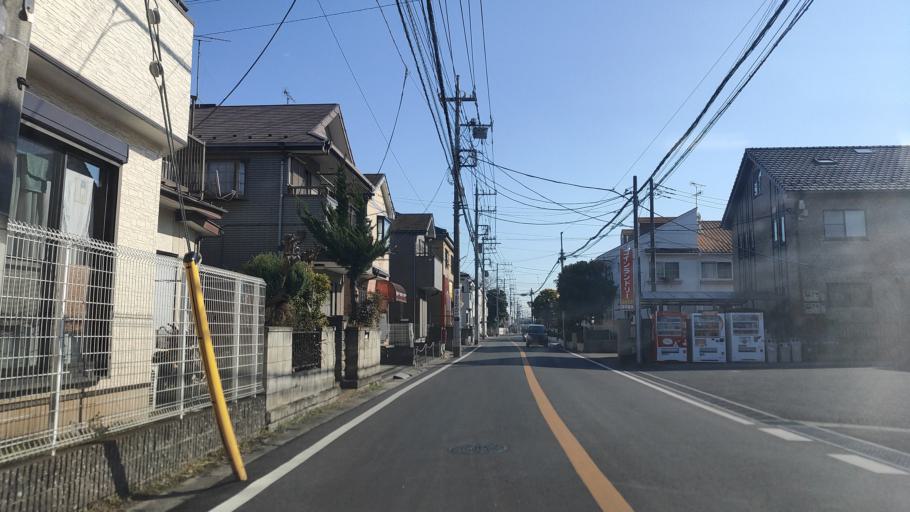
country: JP
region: Chiba
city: Nagareyama
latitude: 35.9037
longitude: 139.9054
